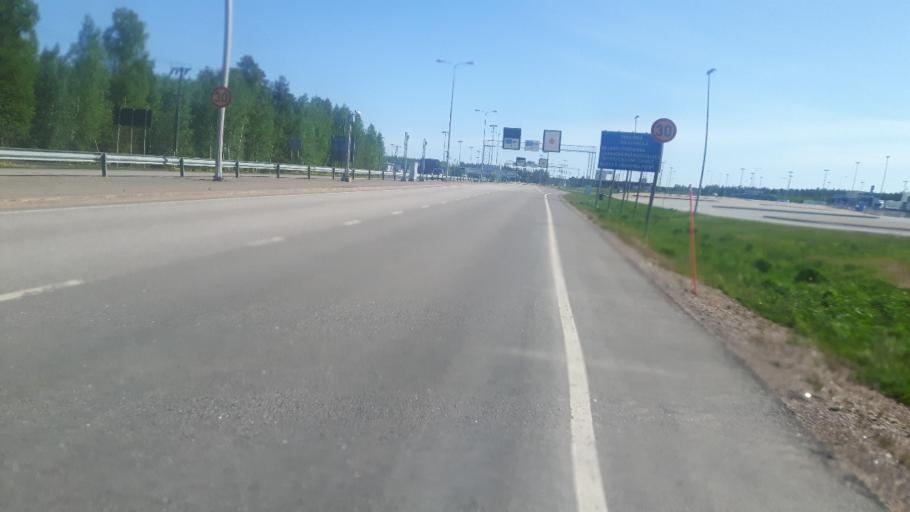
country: FI
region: Kymenlaakso
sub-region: Kotka-Hamina
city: Virojoki
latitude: 60.6027
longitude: 27.8416
